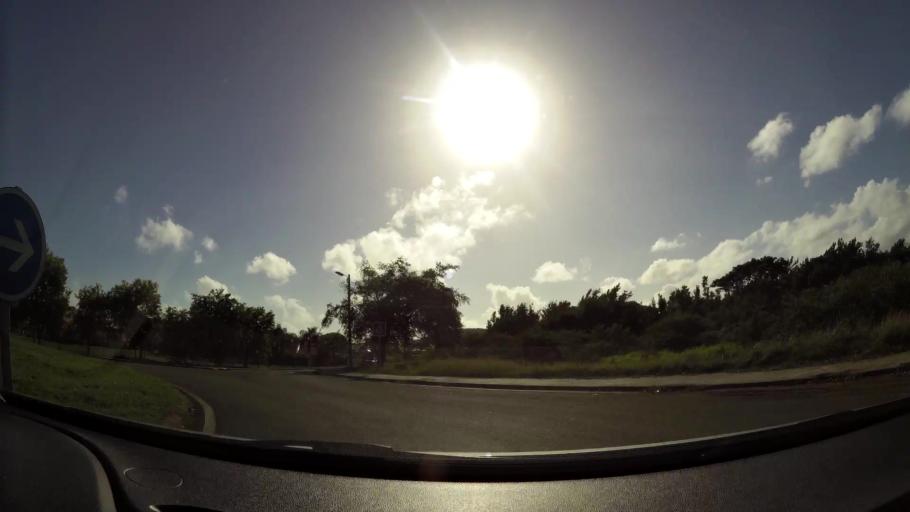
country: MQ
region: Martinique
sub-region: Martinique
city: Le Francois
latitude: 14.6213
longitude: -60.9036
